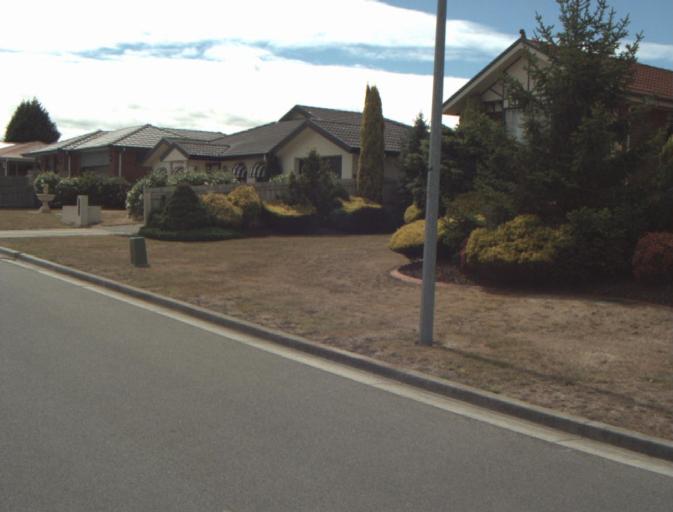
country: AU
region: Tasmania
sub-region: Launceston
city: Mayfield
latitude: -41.3881
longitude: 147.1086
